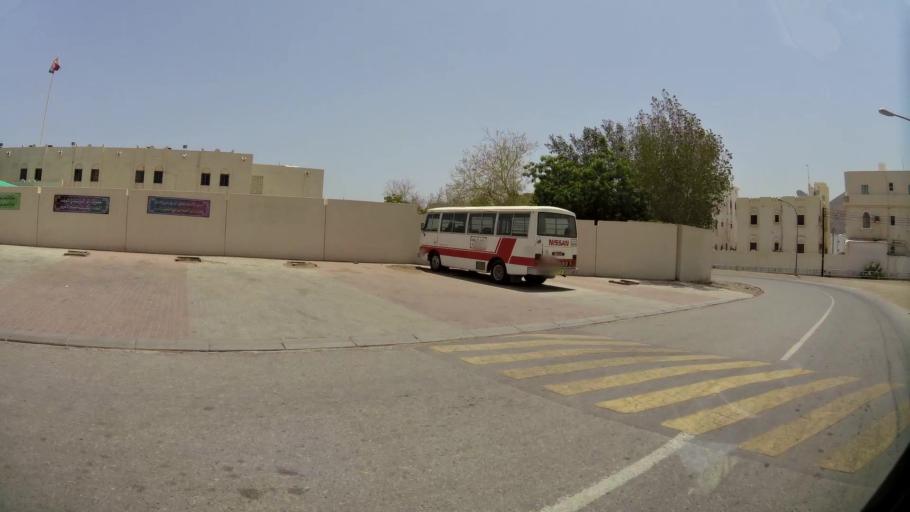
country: OM
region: Muhafazat Masqat
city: Bawshar
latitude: 23.5808
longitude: 58.4267
